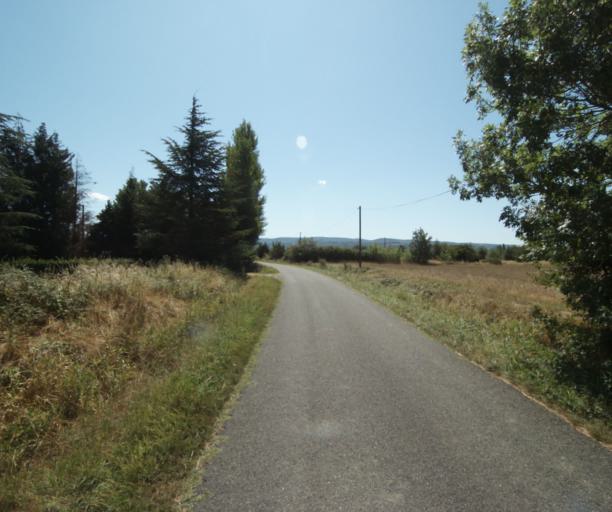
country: FR
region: Midi-Pyrenees
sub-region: Departement de la Haute-Garonne
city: Revel
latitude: 43.4759
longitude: 1.9791
